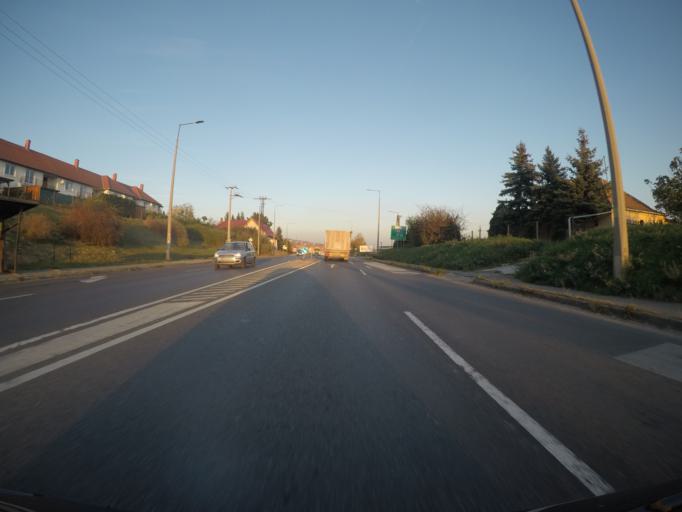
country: HU
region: Baranya
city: Pellerd
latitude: 46.0634
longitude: 18.1538
